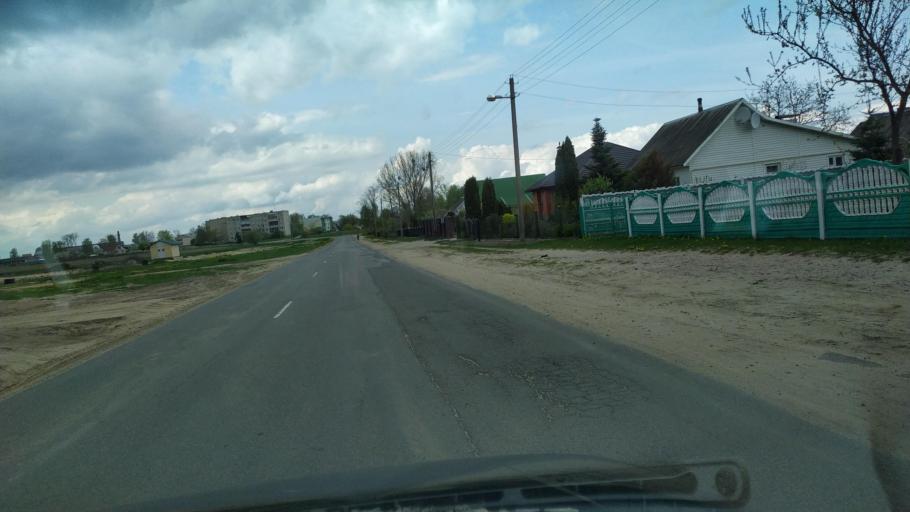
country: BY
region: Brest
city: Pruzhany
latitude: 52.5619
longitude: 24.4248
